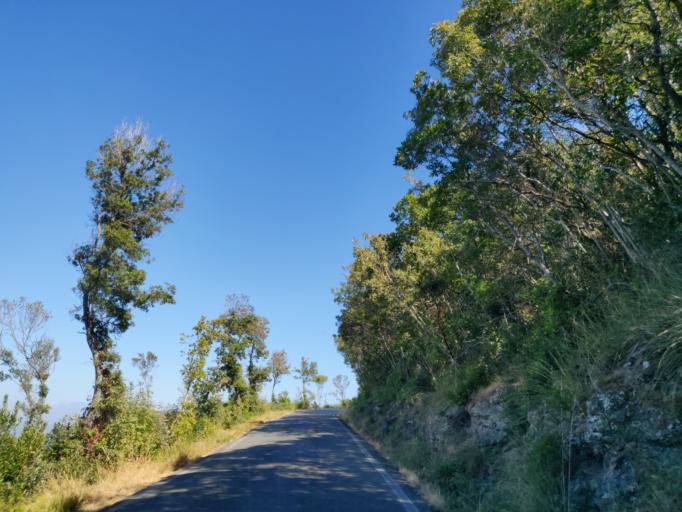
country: IT
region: Tuscany
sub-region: Provincia di Grosseto
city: Monte Argentario
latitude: 42.4212
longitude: 11.1619
